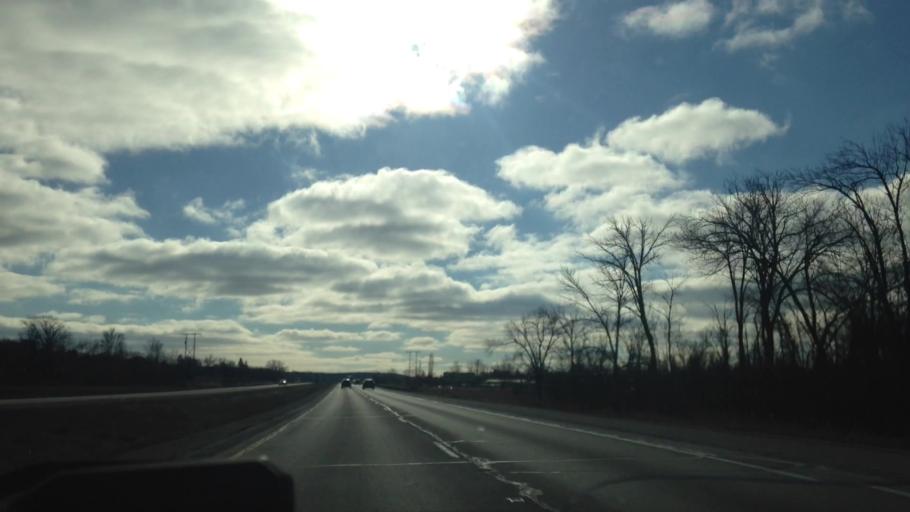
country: US
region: Wisconsin
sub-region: Washington County
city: Slinger
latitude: 43.4024
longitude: -88.3238
